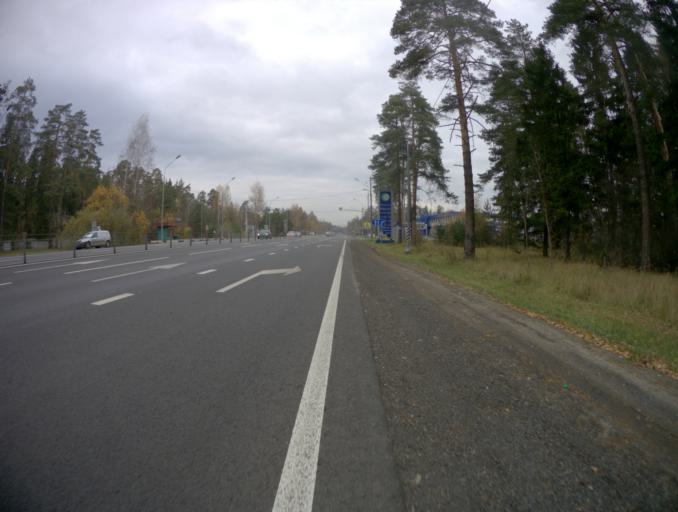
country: RU
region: Moskovskaya
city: Malaya Dubna
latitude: 55.8477
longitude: 38.9646
